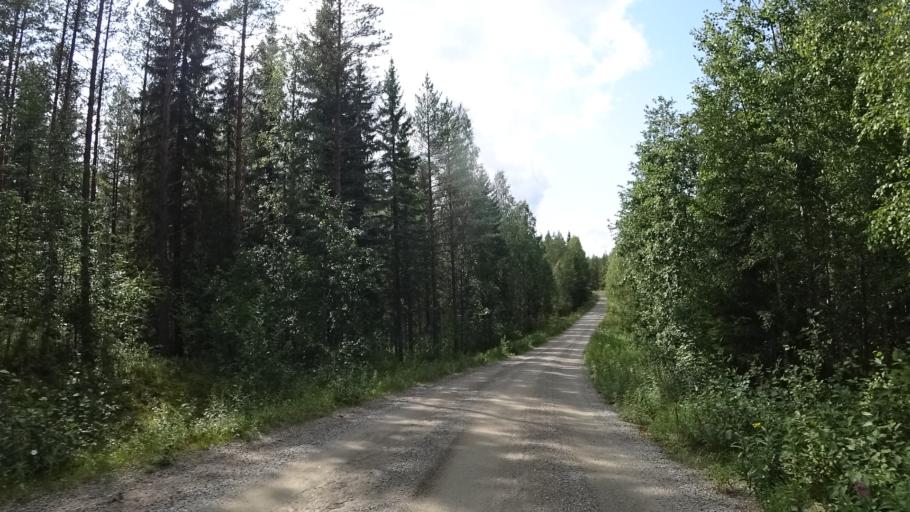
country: FI
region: North Karelia
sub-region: Joensuu
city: Ilomantsi
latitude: 62.9221
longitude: 31.3515
